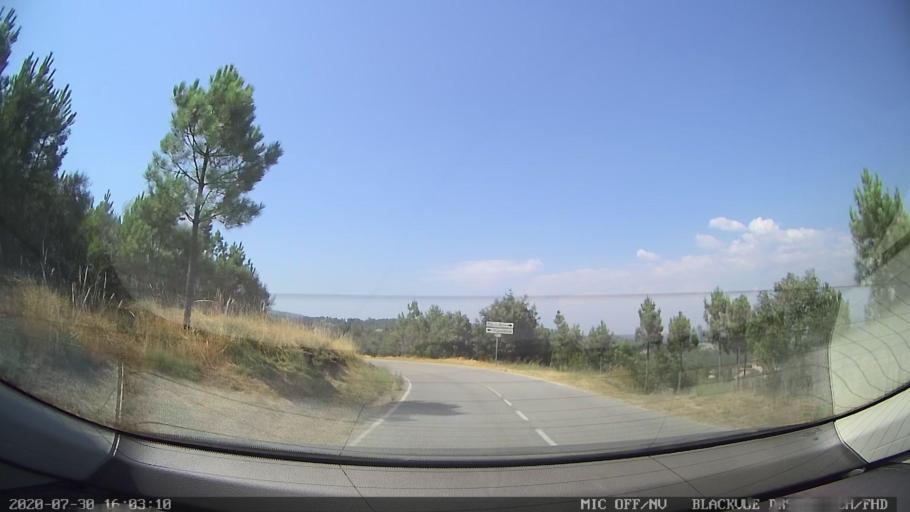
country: PT
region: Vila Real
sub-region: Murca
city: Murca
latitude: 41.3572
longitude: -7.4901
